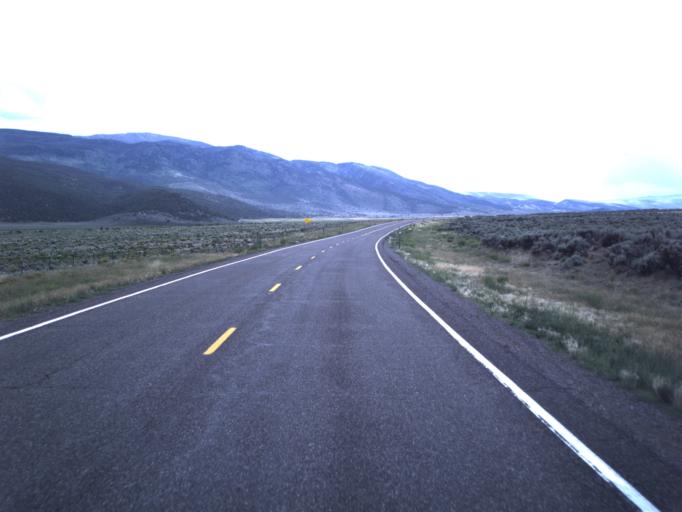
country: US
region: Utah
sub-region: Sevier County
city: Richfield
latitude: 38.6598
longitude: -111.8327
